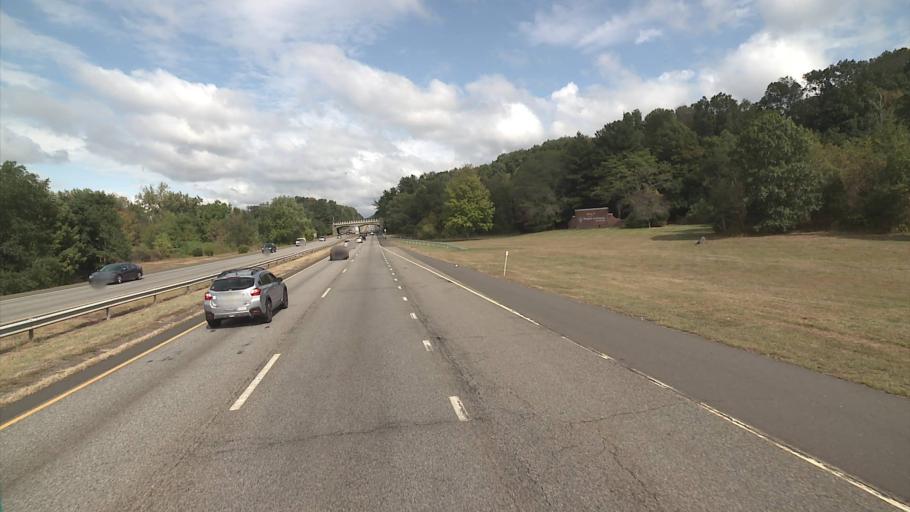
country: US
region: Connecticut
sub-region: New Haven County
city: Wallingford
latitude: 41.4949
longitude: -72.8046
